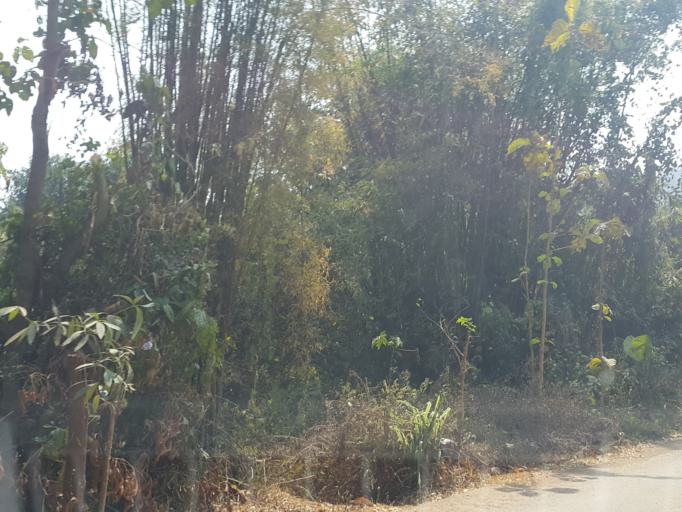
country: TH
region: Chiang Mai
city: Hang Dong
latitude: 18.7505
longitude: 98.8267
